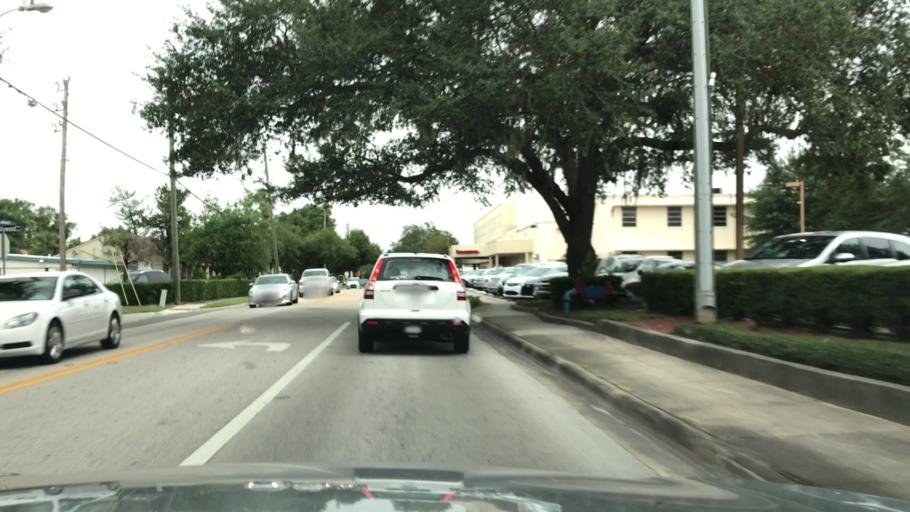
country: US
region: Florida
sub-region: Orange County
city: Winter Park
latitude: 28.5968
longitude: -81.3279
